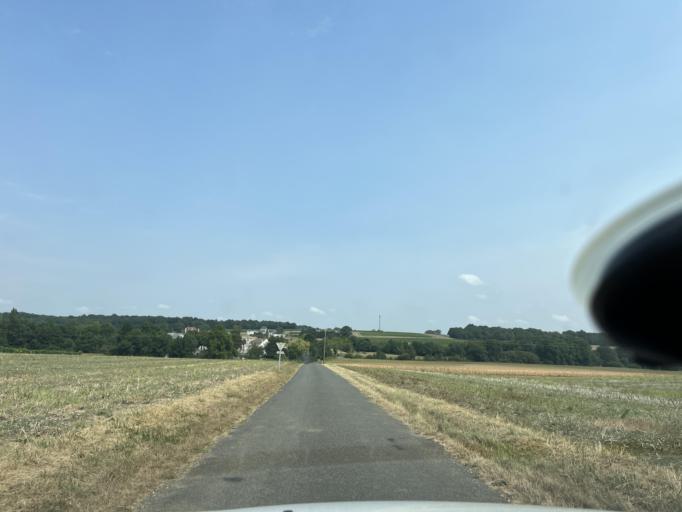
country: FR
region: Poitou-Charentes
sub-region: Departement de la Charente-Maritime
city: Pons
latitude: 45.5875
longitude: -0.5779
